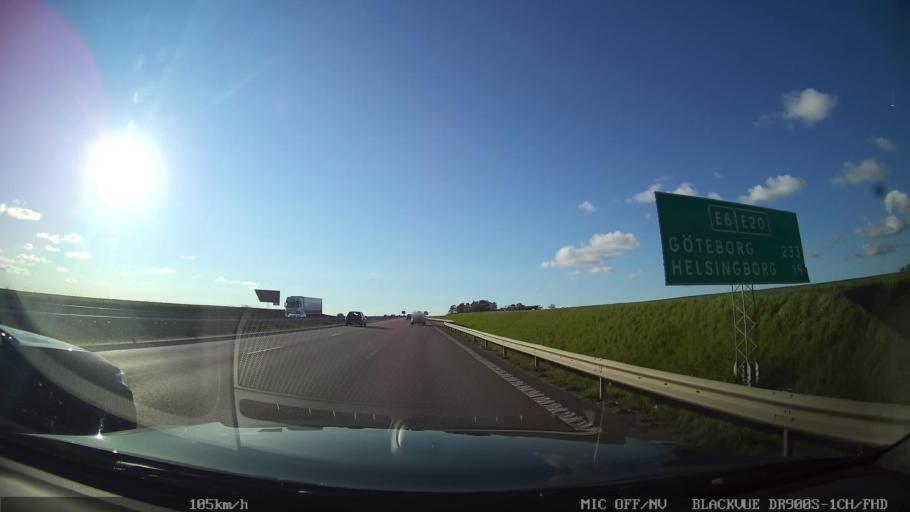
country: SE
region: Skane
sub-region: Helsingborg
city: Glumslov
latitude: 55.9298
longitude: 12.8313
